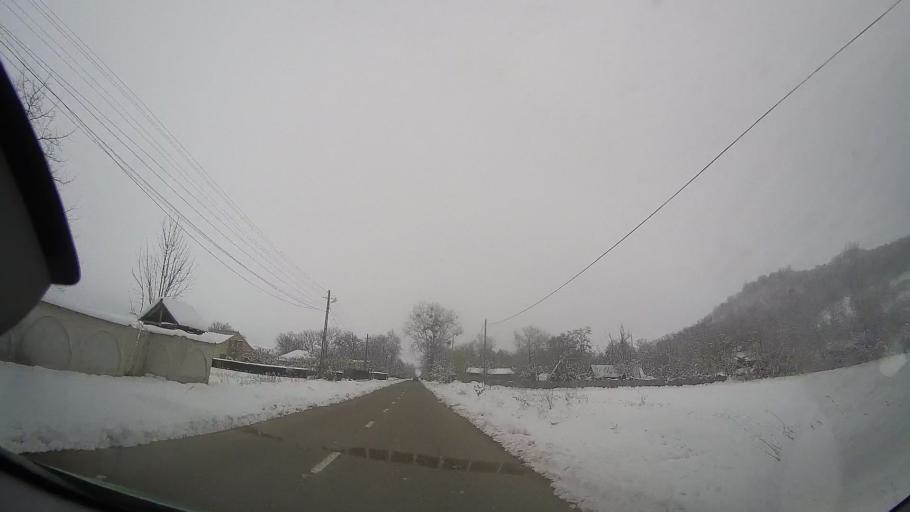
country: RO
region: Neamt
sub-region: Comuna Bozieni
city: Bozieni
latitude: 46.8325
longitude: 27.1660
